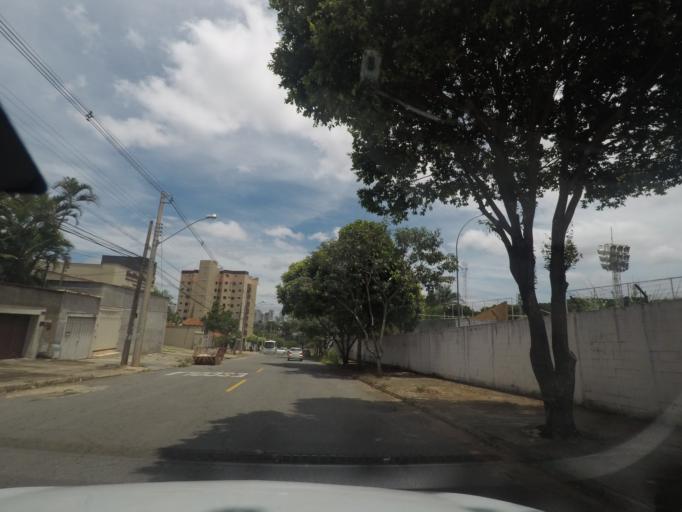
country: BR
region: Goias
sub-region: Goiania
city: Goiania
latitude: -16.6887
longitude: -49.2388
